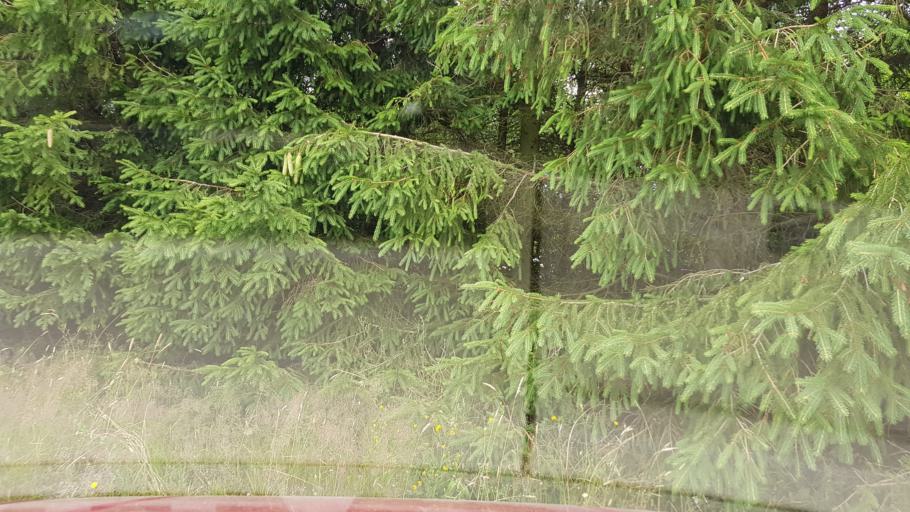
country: PL
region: West Pomeranian Voivodeship
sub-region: Powiat bialogardzki
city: Karlino
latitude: 54.1660
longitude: 15.9236
